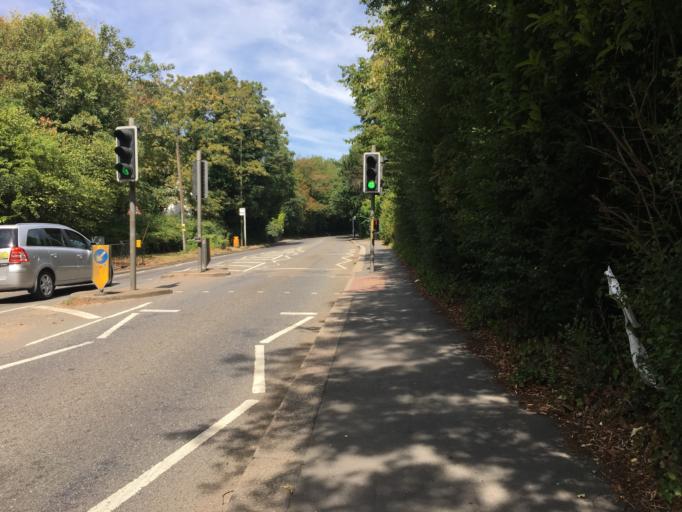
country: GB
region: England
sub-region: Surrey
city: Reigate
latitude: 51.2271
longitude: -0.2012
